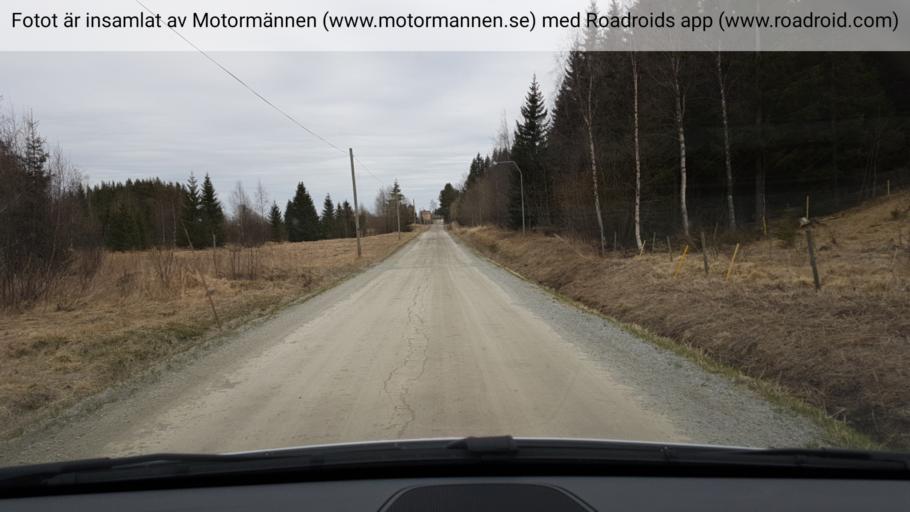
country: SE
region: Jaemtland
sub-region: Bergs Kommun
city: Hoverberg
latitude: 62.9366
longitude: 14.2779
